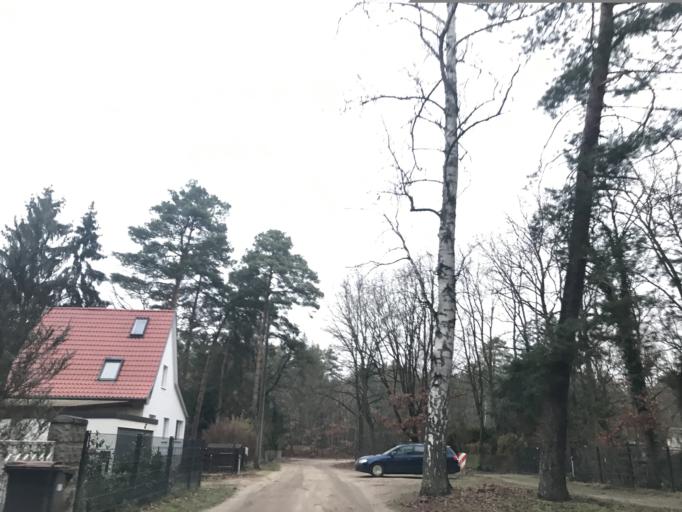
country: DE
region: Brandenburg
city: Falkensee
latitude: 52.5764
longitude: 13.1294
